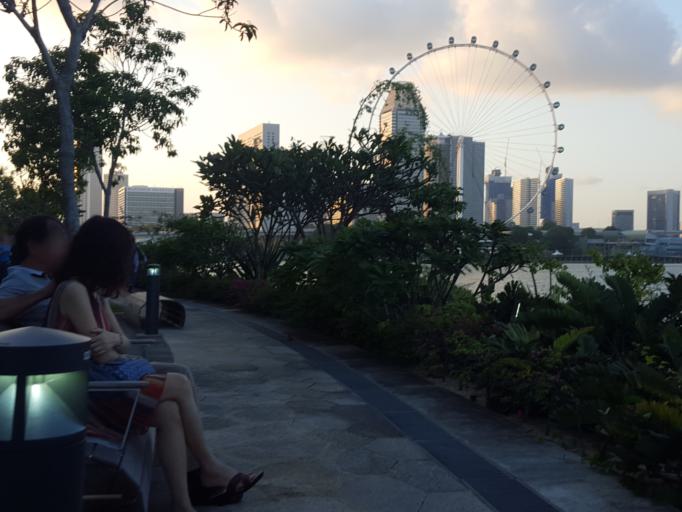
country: SG
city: Singapore
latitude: 1.2842
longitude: 103.8663
